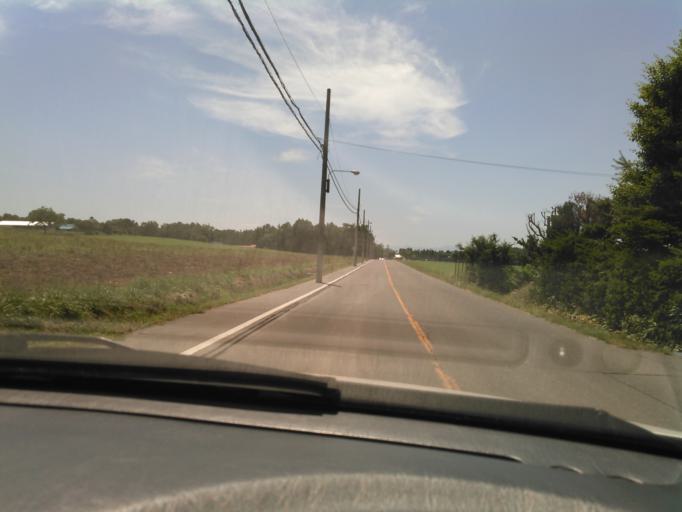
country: JP
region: Hokkaido
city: Ebetsu
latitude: 43.0812
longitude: 141.5189
